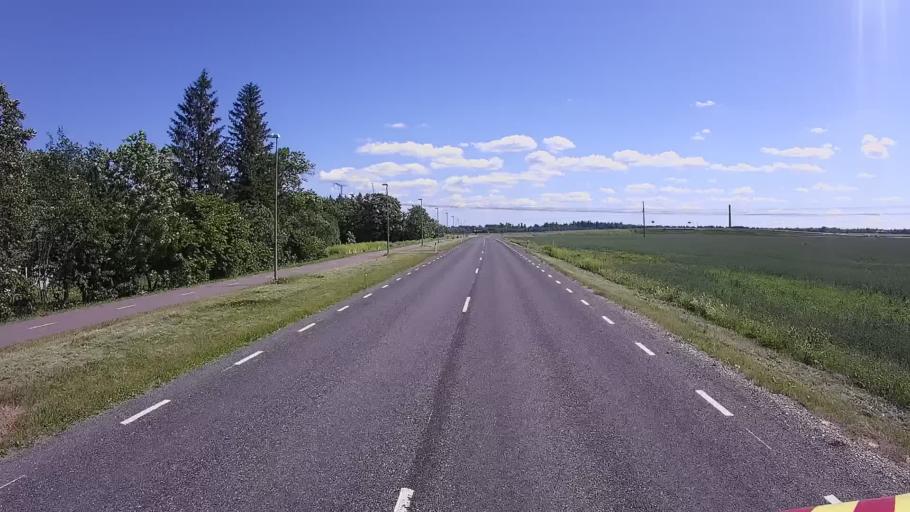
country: EE
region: Ida-Virumaa
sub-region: Kohtla-Jaerve linn
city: Kohtla-Jarve
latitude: 59.3919
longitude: 27.3463
